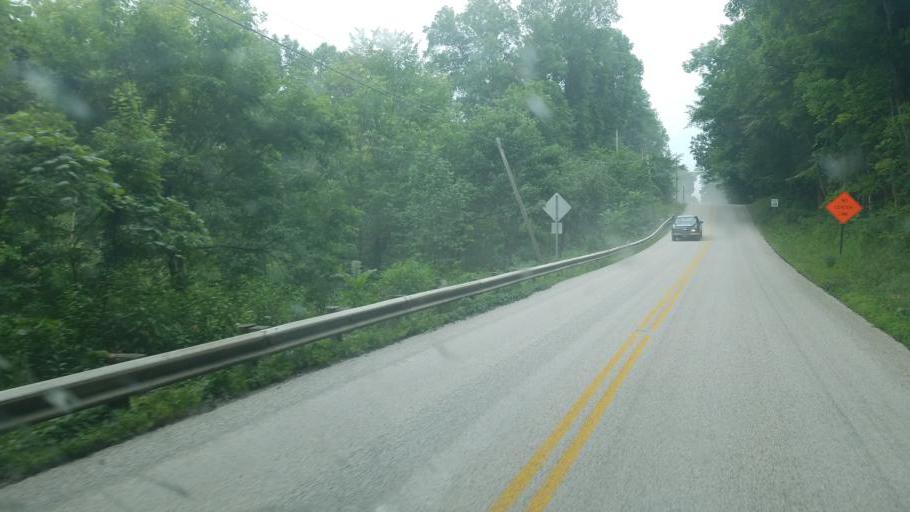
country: US
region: Ohio
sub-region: Trumbull County
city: South Canal
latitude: 41.1515
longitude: -81.0513
